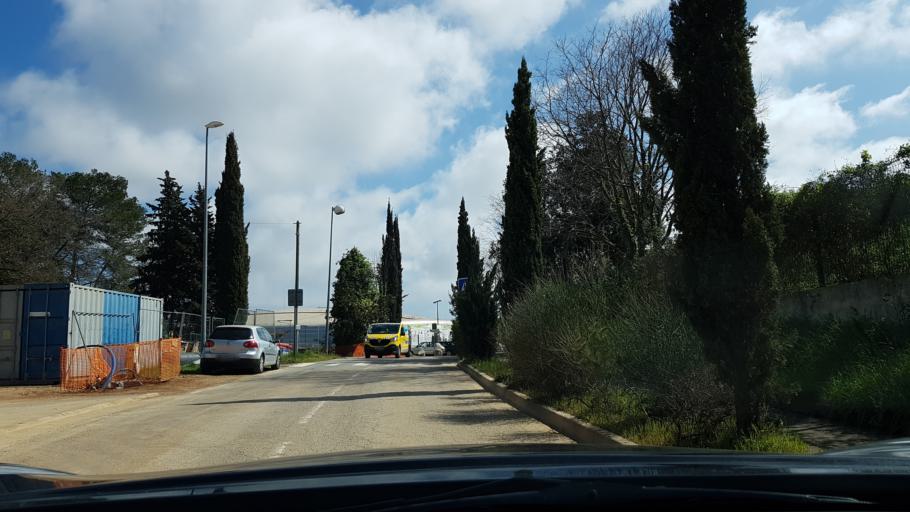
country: FR
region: Provence-Alpes-Cote d'Azur
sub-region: Departement des Alpes-Maritimes
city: Biot
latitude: 43.6076
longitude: 7.0752
